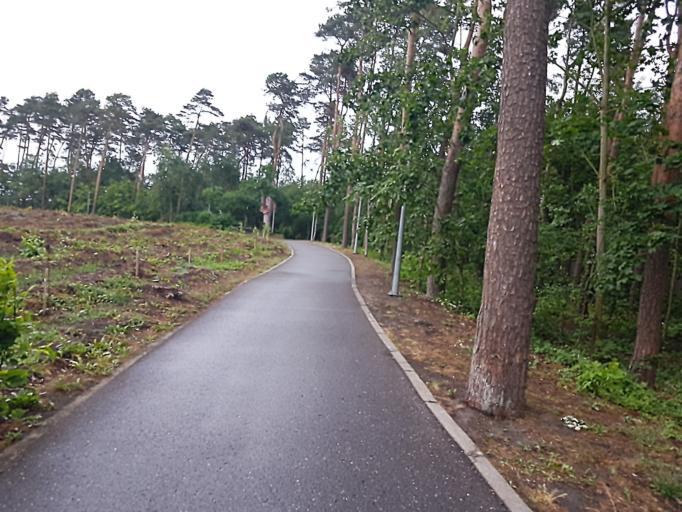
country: PL
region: Greater Poland Voivodeship
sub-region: Powiat koninski
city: Lichen Stary
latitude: 52.2961
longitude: 18.3599
